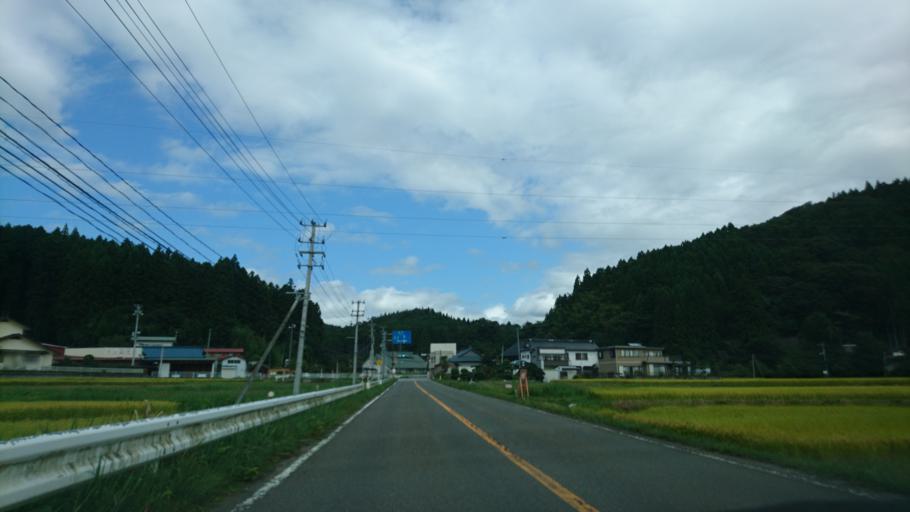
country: JP
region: Miyagi
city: Furukawa
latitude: 38.7656
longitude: 140.8635
